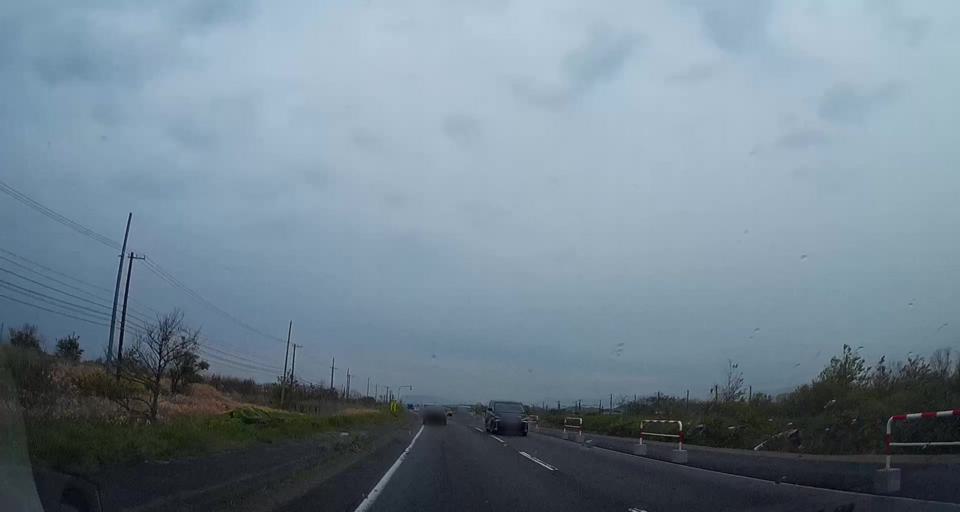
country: JP
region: Hokkaido
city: Shiraoi
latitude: 42.5822
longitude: 141.4294
